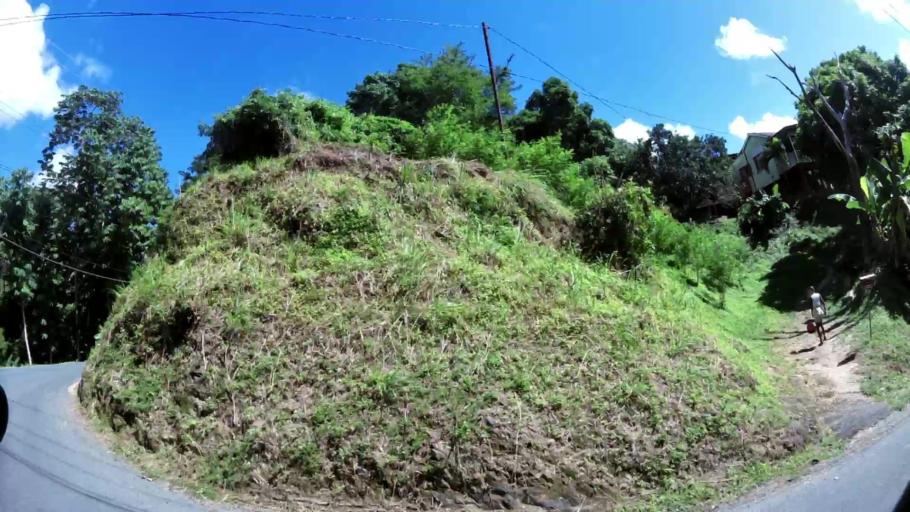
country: TT
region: Tobago
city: Scarborough
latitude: 11.2271
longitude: -60.7463
